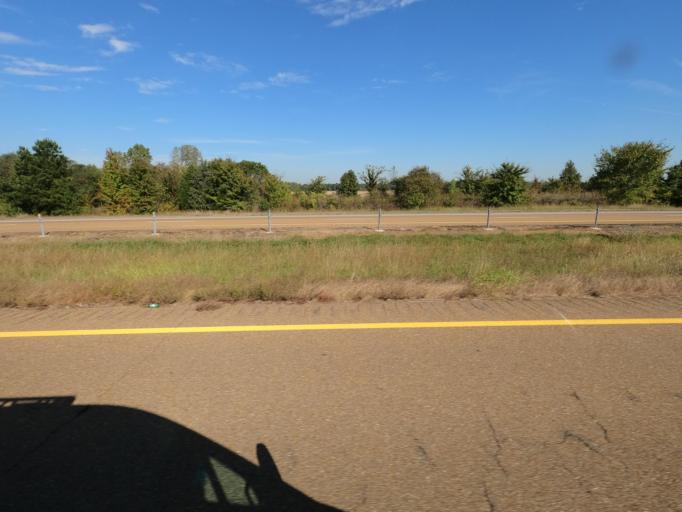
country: US
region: Tennessee
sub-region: Shelby County
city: Lakeland
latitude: 35.3077
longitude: -89.7953
